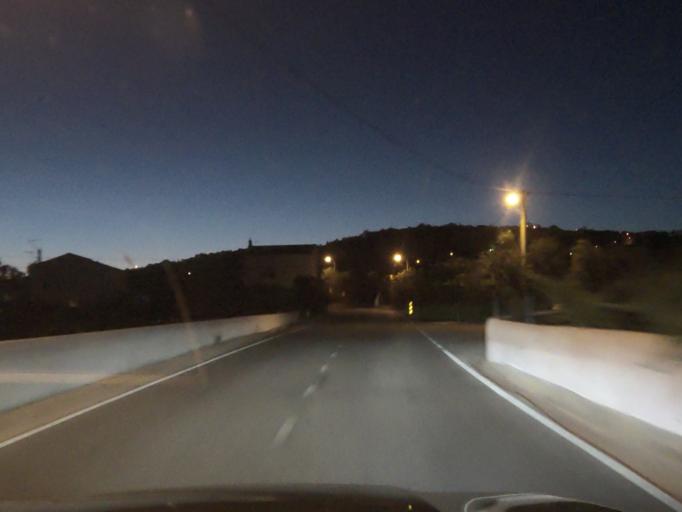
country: PT
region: Faro
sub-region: Loule
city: Loule
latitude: 37.1435
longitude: -8.0103
